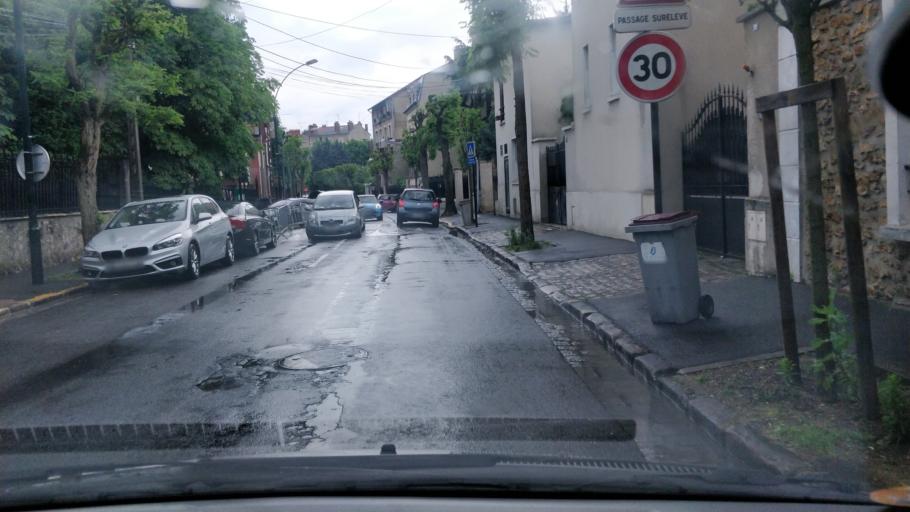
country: FR
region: Ile-de-France
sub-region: Departement de Seine-Saint-Denis
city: Le Raincy
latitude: 48.8943
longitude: 2.5090
